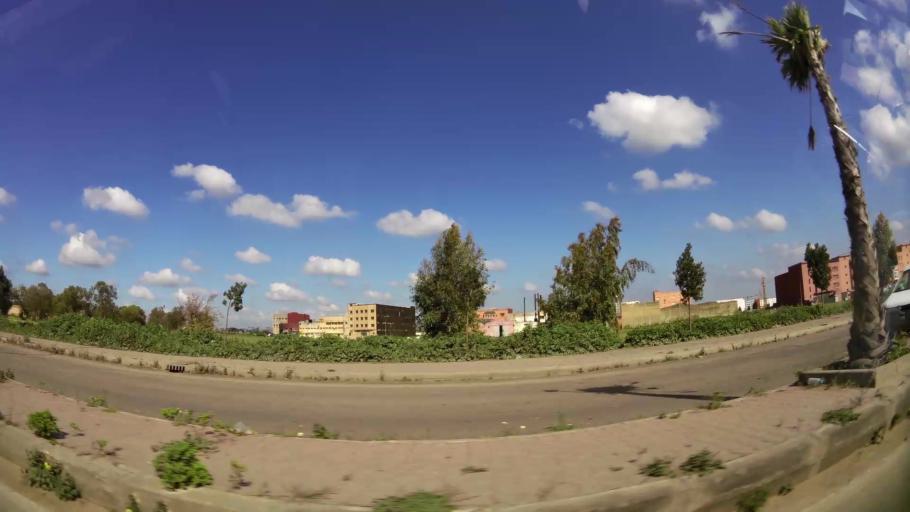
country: MA
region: Grand Casablanca
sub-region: Mediouna
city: Mediouna
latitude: 33.4485
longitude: -7.5212
